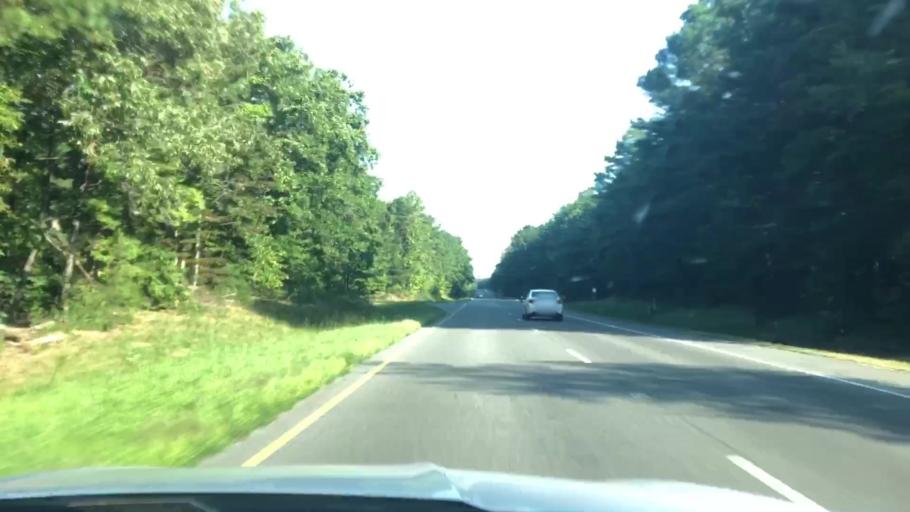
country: US
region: Virginia
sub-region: King and Queen County
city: King and Queen Court House
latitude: 37.7902
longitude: -76.7673
